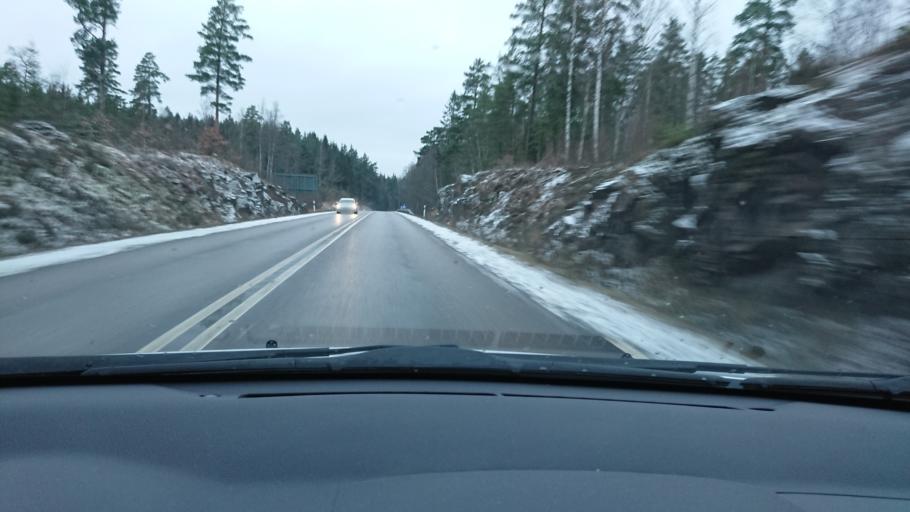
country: SE
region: Kalmar
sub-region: Hultsfreds Kommun
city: Hultsfred
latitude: 57.4916
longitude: 15.8240
